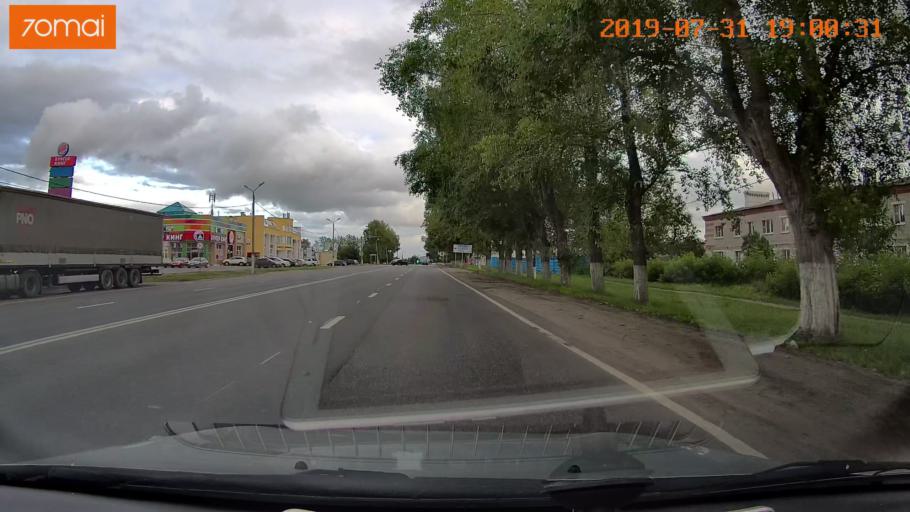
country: RU
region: Moskovskaya
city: Raduzhnyy
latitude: 55.1327
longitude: 38.7248
